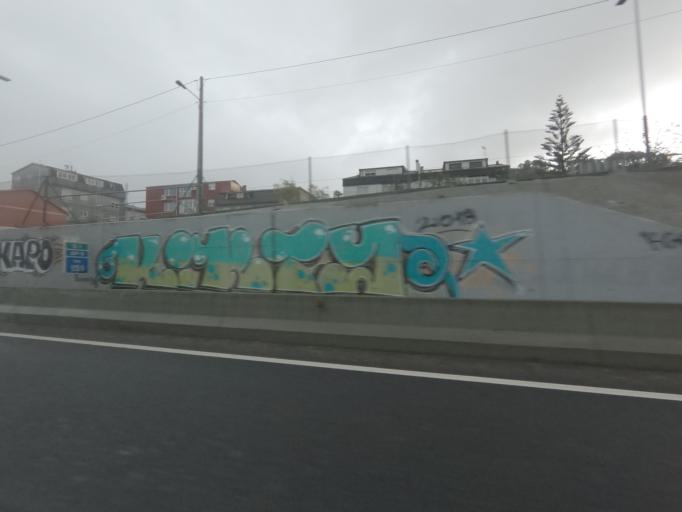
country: ES
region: Galicia
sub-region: Provincia de Pontevedra
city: Vigo
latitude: 42.2771
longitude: -8.6932
